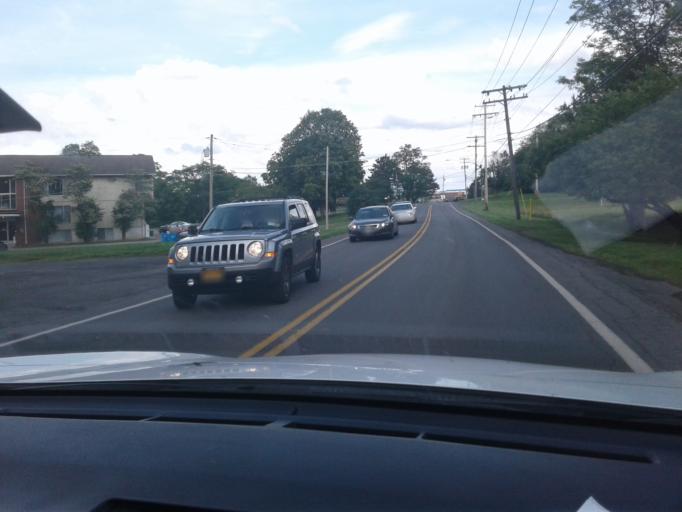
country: US
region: New York
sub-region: Onondaga County
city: East Syracuse
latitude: 43.0447
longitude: -76.0726
